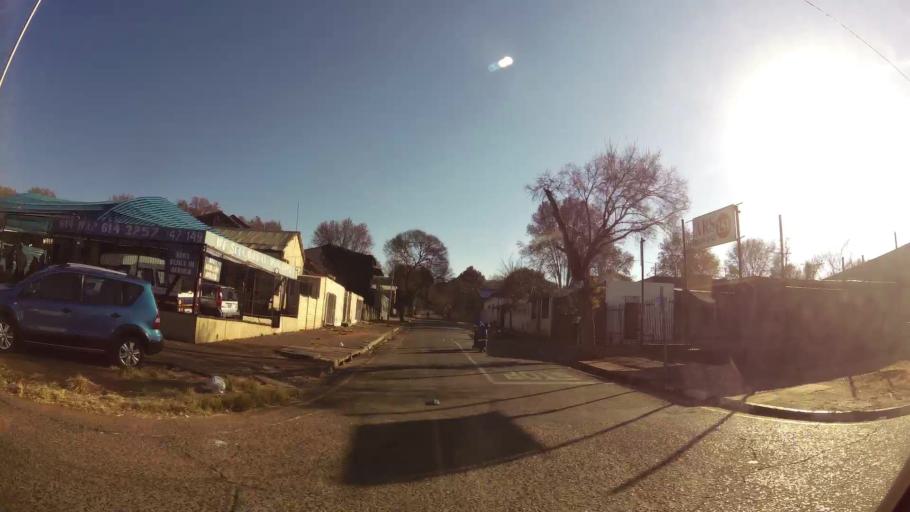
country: ZA
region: Gauteng
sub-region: City of Johannesburg Metropolitan Municipality
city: Johannesburg
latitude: -26.2056
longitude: 28.0771
